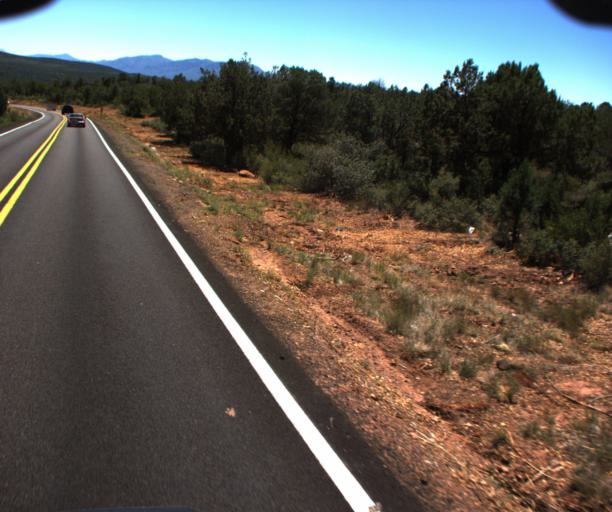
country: US
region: Arizona
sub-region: Gila County
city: Pine
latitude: 34.3456
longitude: -111.4262
